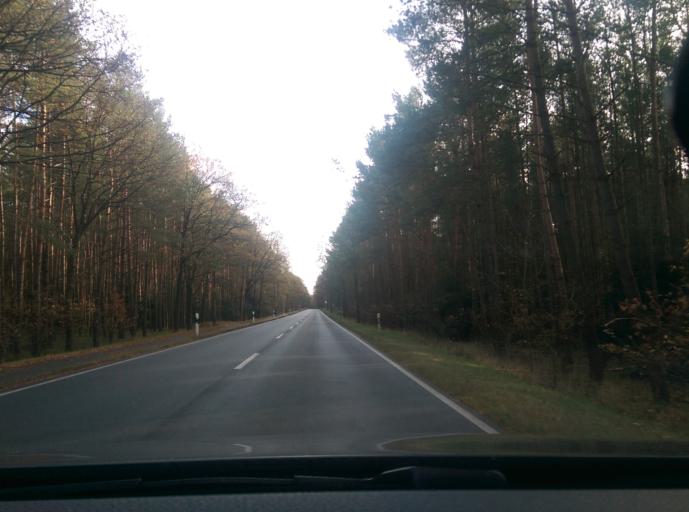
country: DE
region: Lower Saxony
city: Hambuhren
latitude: 52.6713
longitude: 9.9626
